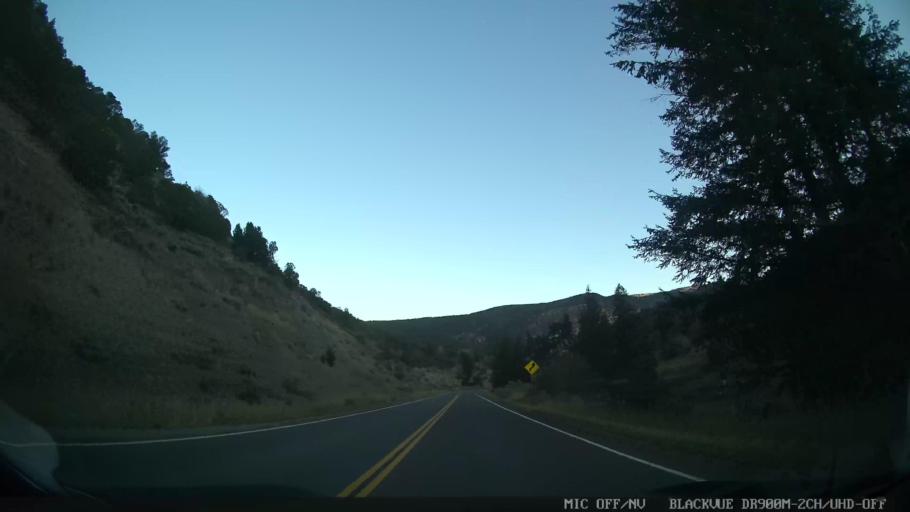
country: US
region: Colorado
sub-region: Eagle County
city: Edwards
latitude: 39.8517
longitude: -106.6446
